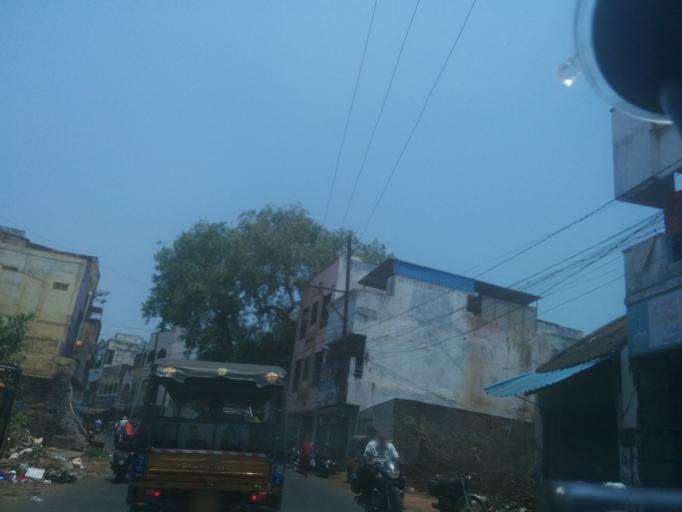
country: IN
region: Andhra Pradesh
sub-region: East Godavari
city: Rajahmundry
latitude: 17.0001
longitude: 81.7759
